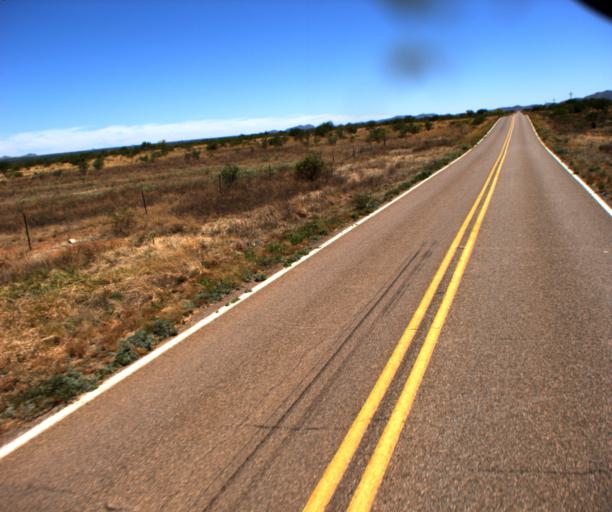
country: US
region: Arizona
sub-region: Pima County
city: Arivaca Junction
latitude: 31.6248
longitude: -111.5112
